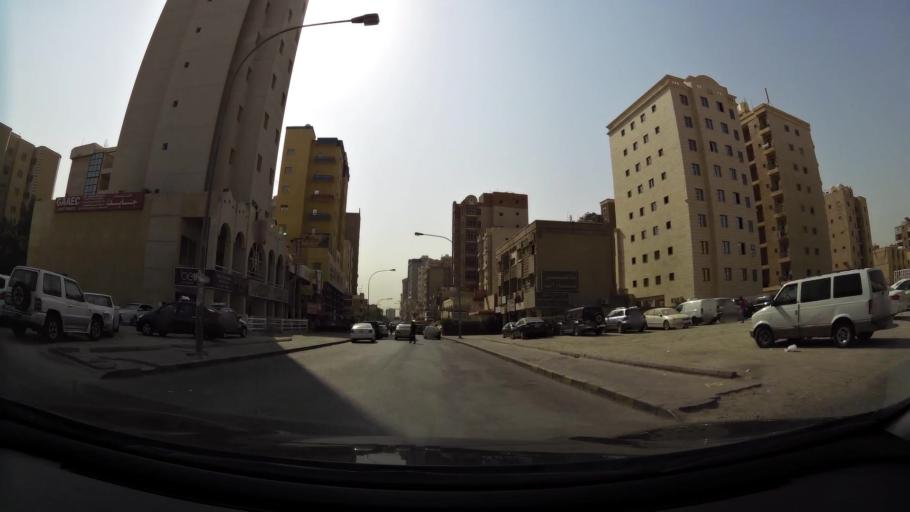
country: KW
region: Muhafazat Hawalli
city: Hawalli
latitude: 29.3317
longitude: 48.0184
